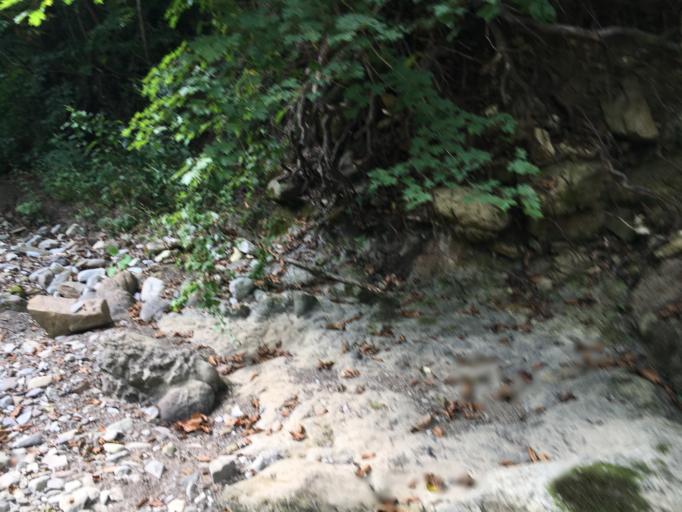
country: RU
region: Krasnodarskiy
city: Tuapse
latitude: 44.2559
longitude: 39.2187
